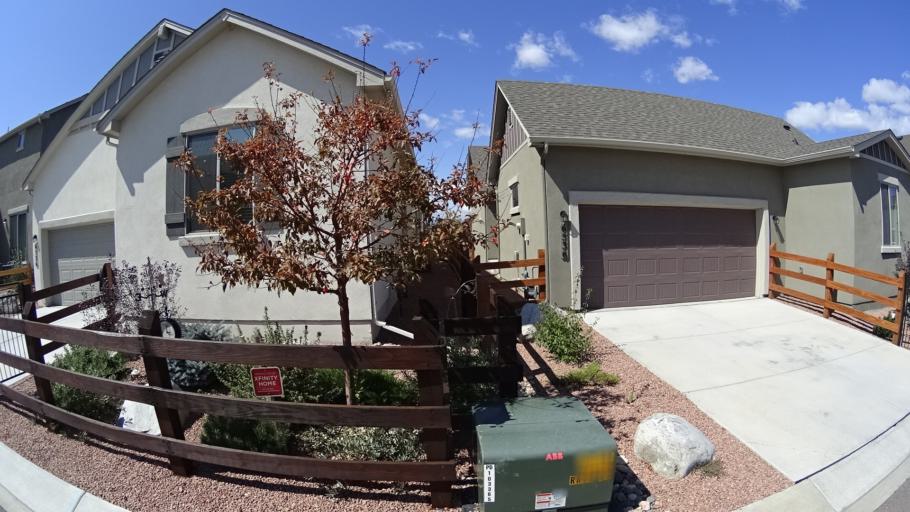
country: US
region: Colorado
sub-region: El Paso County
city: Cimarron Hills
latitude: 38.9273
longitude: -104.6862
